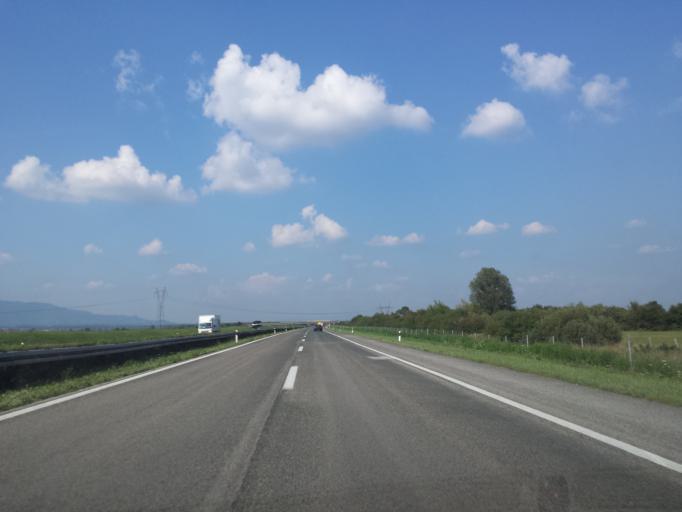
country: HR
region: Zagrebacka
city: Jastrebarsko
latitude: 45.6198
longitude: 15.6493
